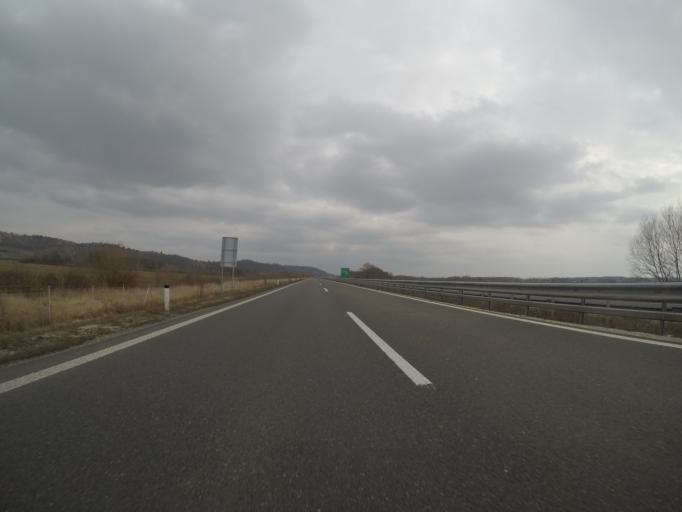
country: HR
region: Medimurska
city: Peklenica
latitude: 46.5272
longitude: 16.5004
